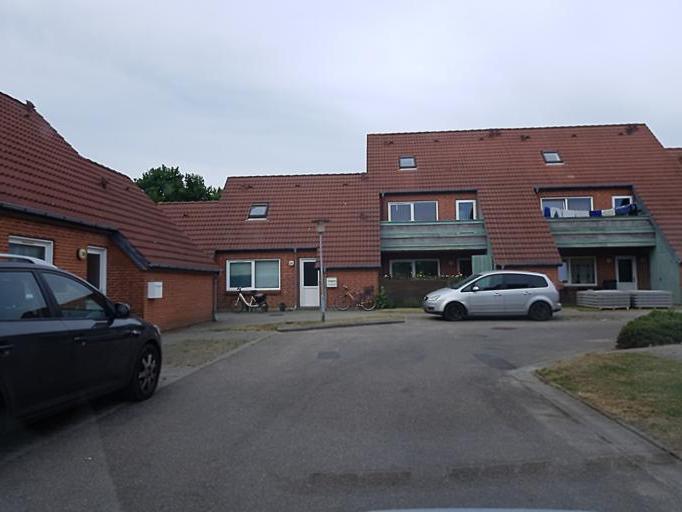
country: DK
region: South Denmark
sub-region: Esbjerg Kommune
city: Esbjerg
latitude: 55.5169
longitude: 8.4200
